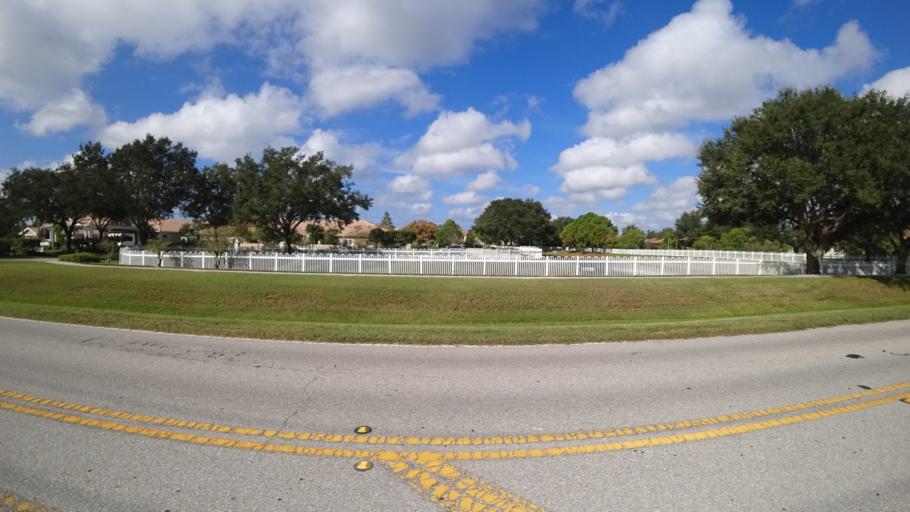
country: US
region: Florida
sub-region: Sarasota County
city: North Sarasota
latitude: 27.3955
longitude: -82.5136
